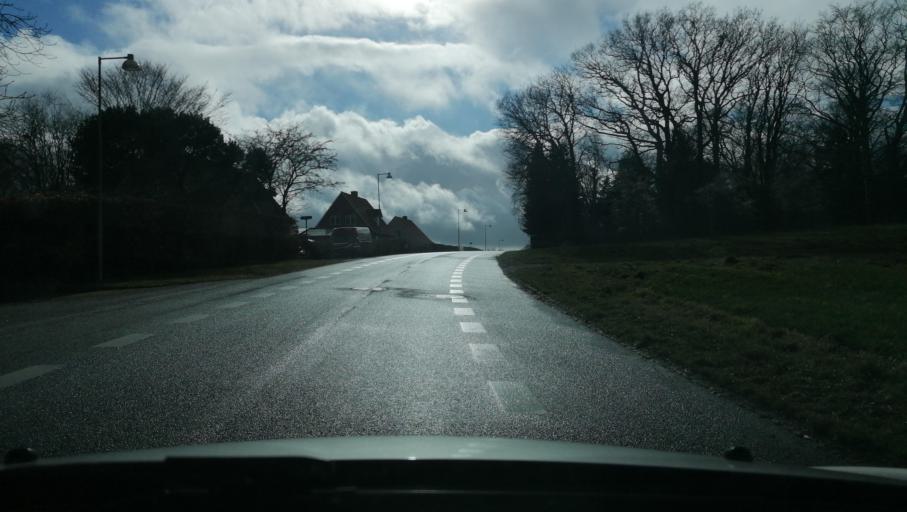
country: DK
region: Zealand
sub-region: Odsherred Kommune
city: Horve
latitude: 55.7442
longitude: 11.4250
